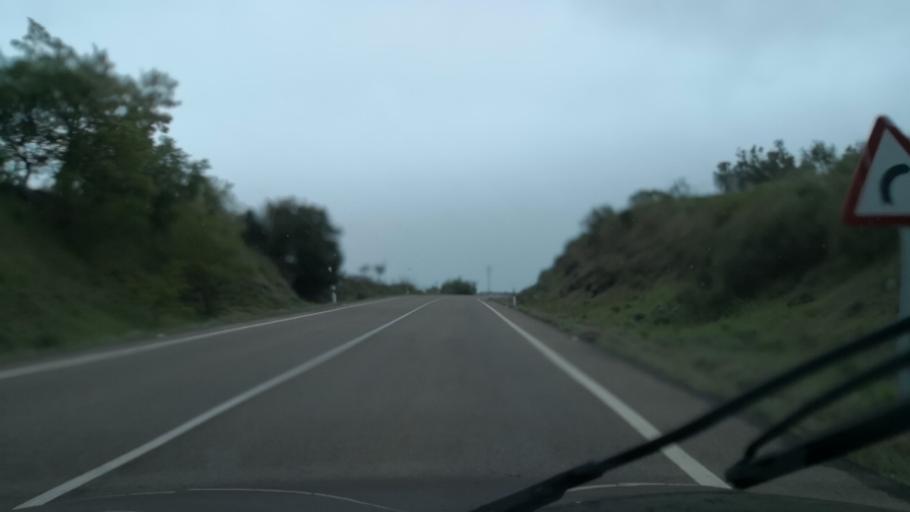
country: ES
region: Extremadura
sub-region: Provincia de Badajoz
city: La Roca de la Sierra
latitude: 39.1112
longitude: -6.6926
